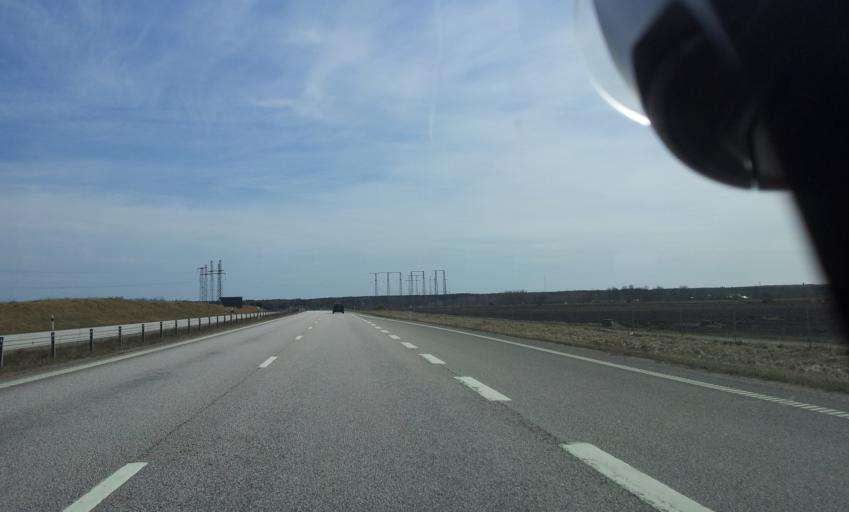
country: SE
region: Uppsala
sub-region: Tierps Kommun
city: Tierp
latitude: 60.3365
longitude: 17.4909
